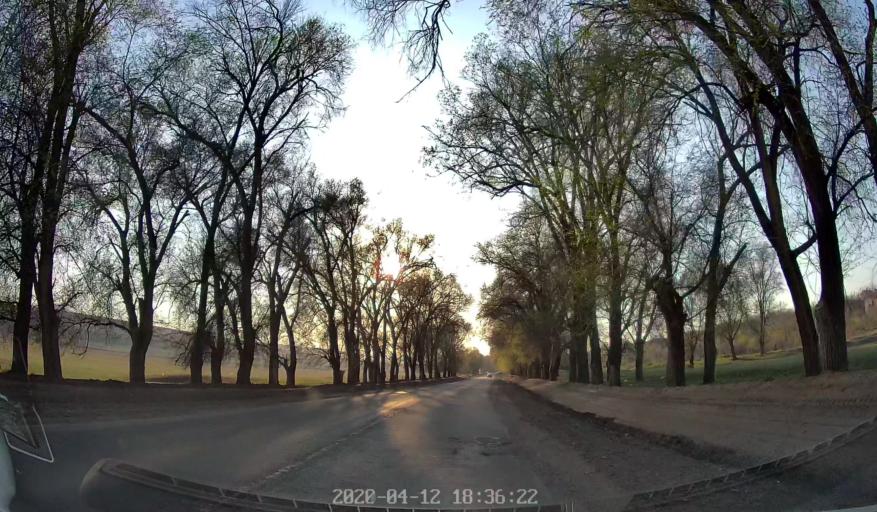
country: MD
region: Chisinau
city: Vadul lui Voda
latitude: 47.1167
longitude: 29.0315
